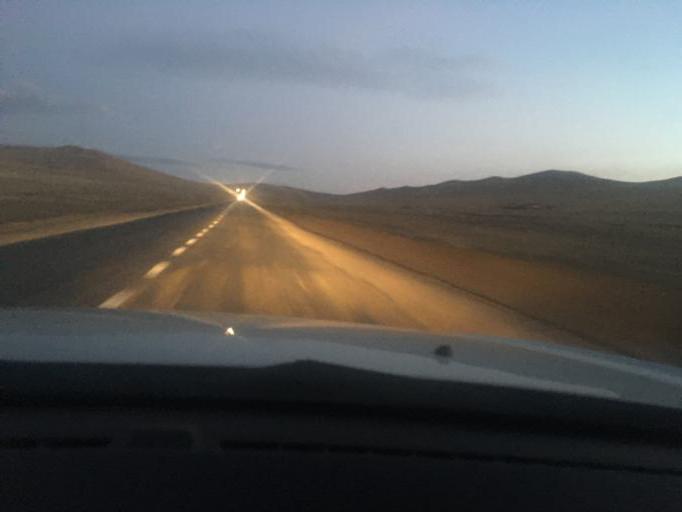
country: MN
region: Ulaanbaatar
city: Ulaanbaatar
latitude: 47.9846
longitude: 106.5659
